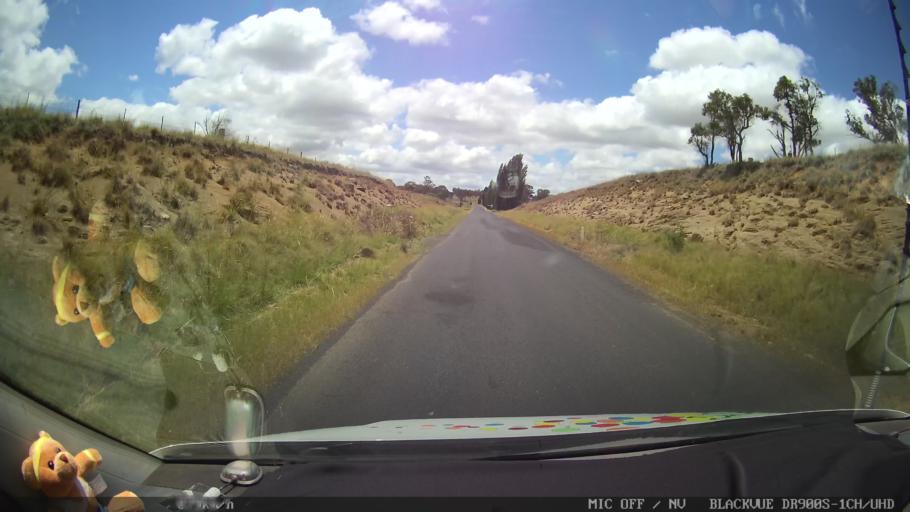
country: AU
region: New South Wales
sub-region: Glen Innes Severn
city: Glen Innes
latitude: -29.4372
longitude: 151.7604
